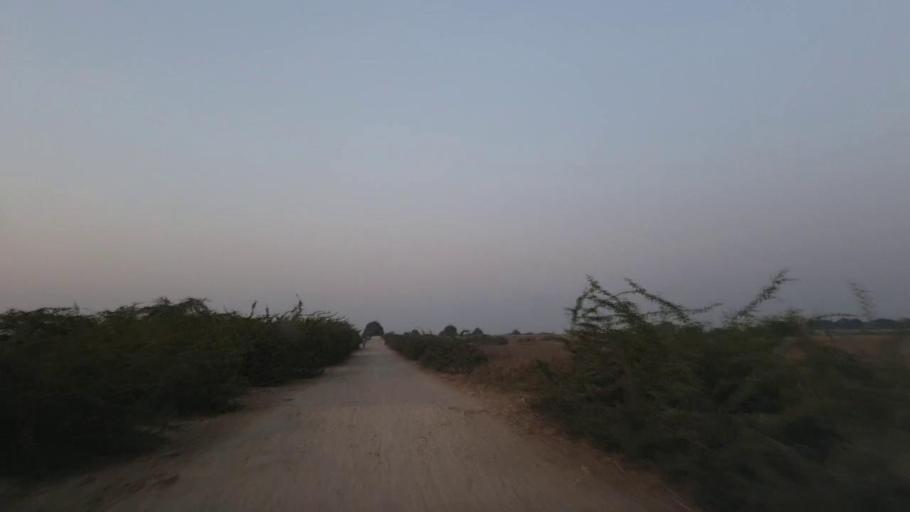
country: PK
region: Sindh
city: Naukot
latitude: 24.9994
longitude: 69.4246
